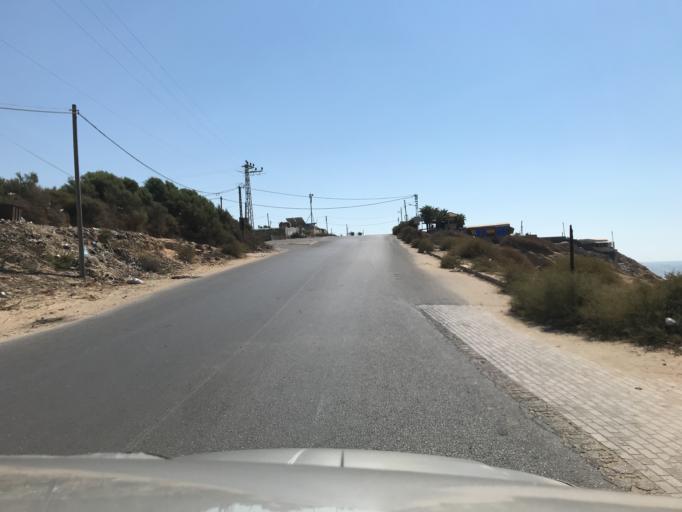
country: PS
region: Gaza Strip
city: Az Zuwaydah
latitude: 31.4582
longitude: 34.3707
